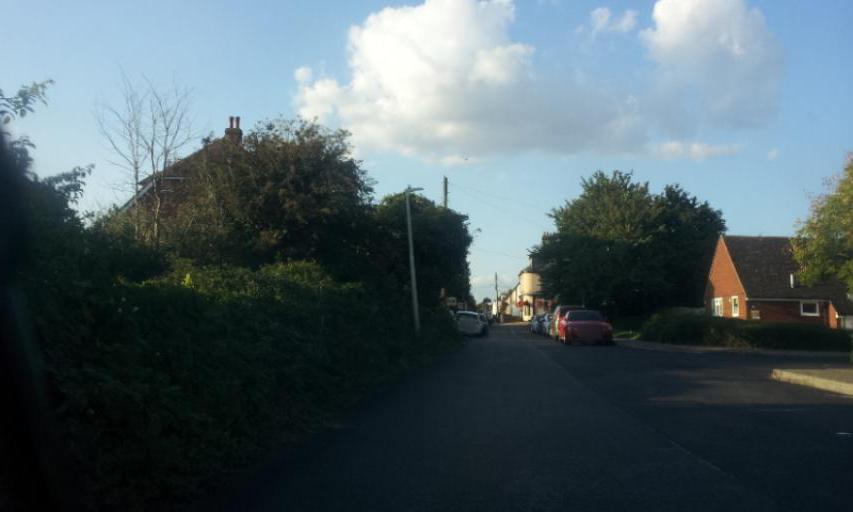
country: GB
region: England
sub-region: Medway
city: Halling
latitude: 51.3463
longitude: 0.4579
